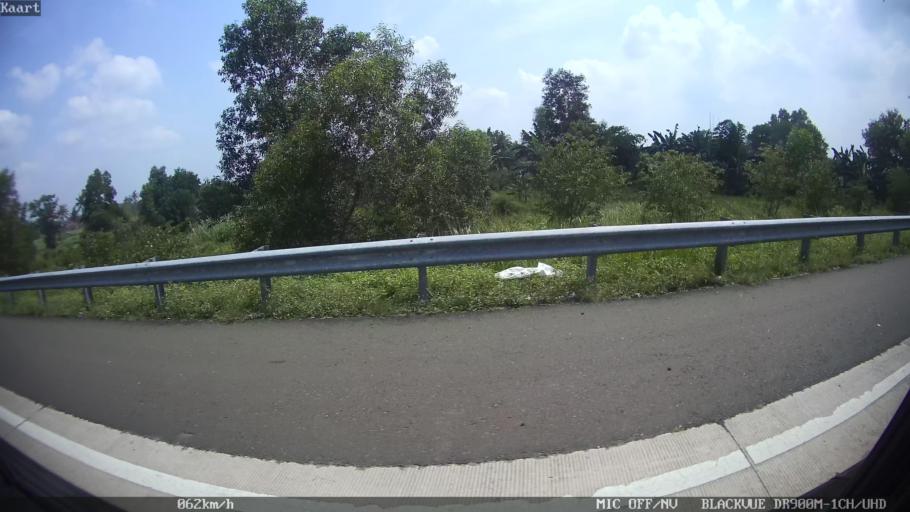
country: ID
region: Lampung
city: Kedaton
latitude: -5.3368
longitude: 105.3032
